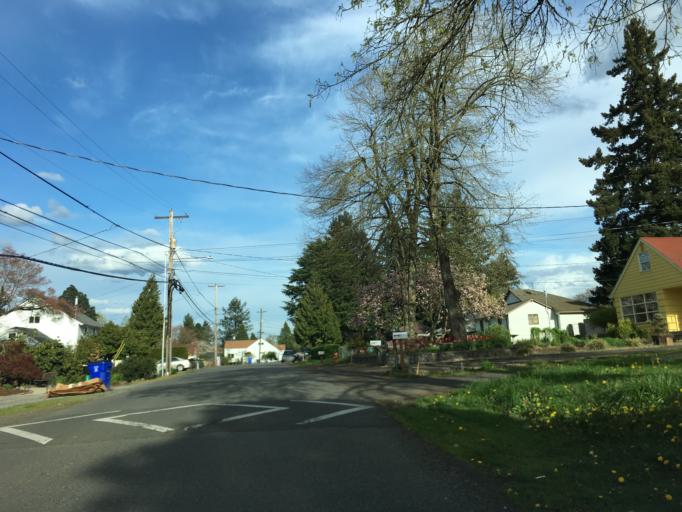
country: US
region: Oregon
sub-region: Multnomah County
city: Lents
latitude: 45.5435
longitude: -122.5541
